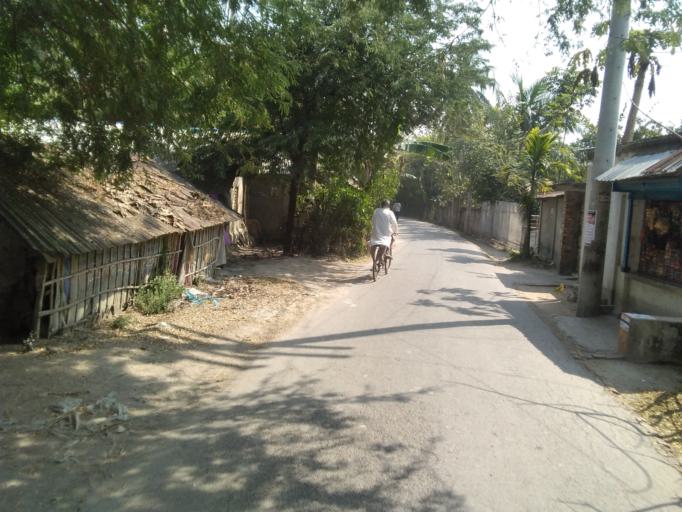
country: IN
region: West Bengal
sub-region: North 24 Parganas
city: Taki
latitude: 22.5908
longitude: 88.9960
